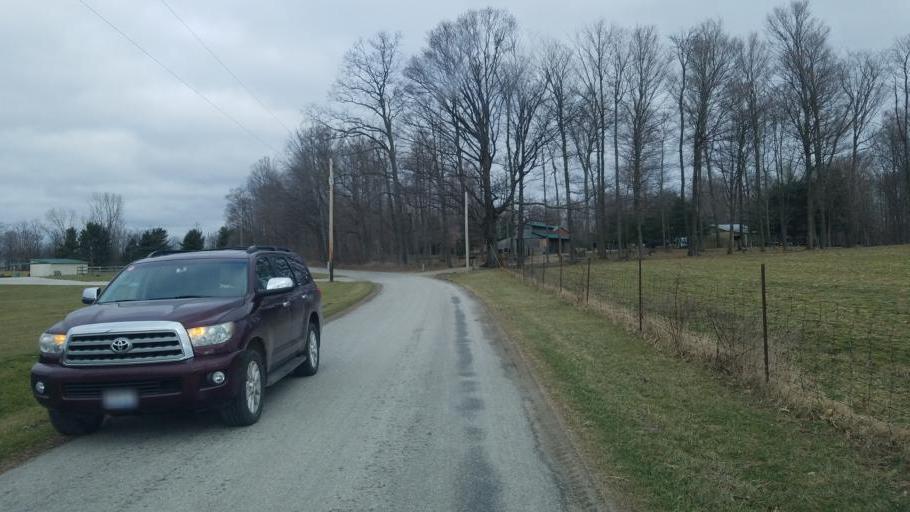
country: US
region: Ohio
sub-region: Morrow County
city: Mount Gilead
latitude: 40.5699
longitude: -82.6972
